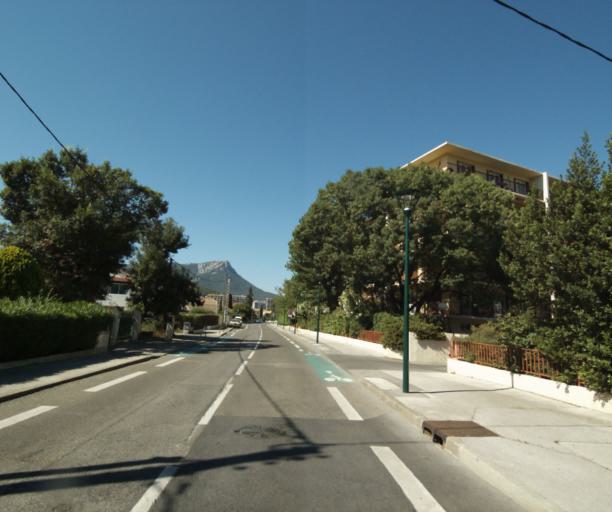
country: FR
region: Provence-Alpes-Cote d'Azur
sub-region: Departement du Var
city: La Garde
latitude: 43.1207
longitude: 6.0064
